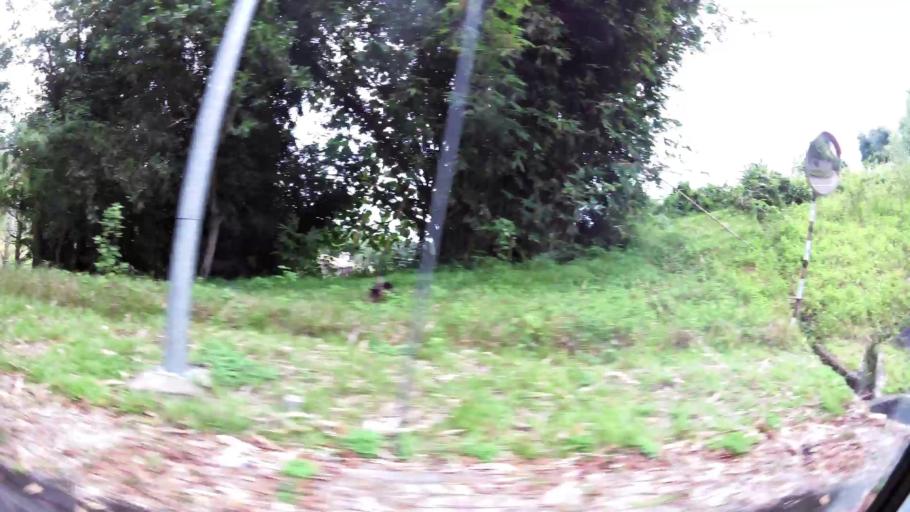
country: BN
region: Brunei and Muara
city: Bandar Seri Begawan
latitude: 4.8813
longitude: 114.9241
